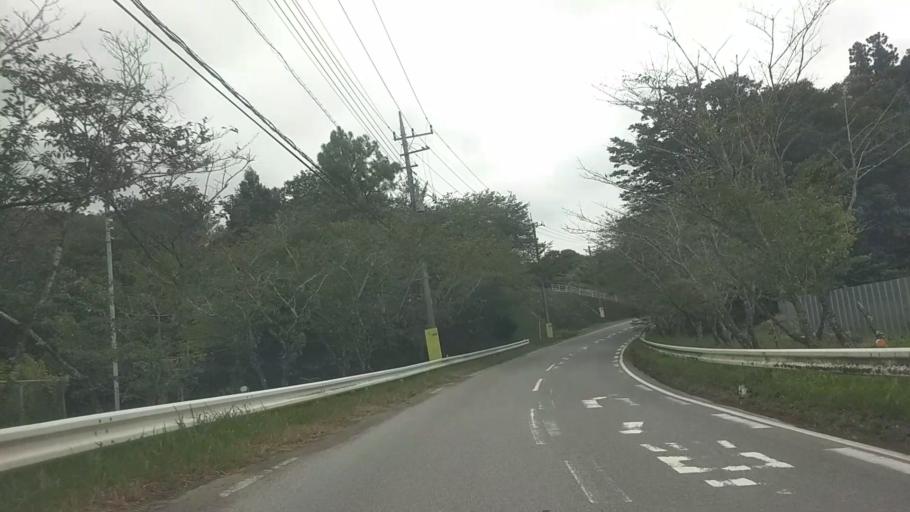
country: JP
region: Chiba
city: Kimitsu
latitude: 35.2277
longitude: 139.9589
